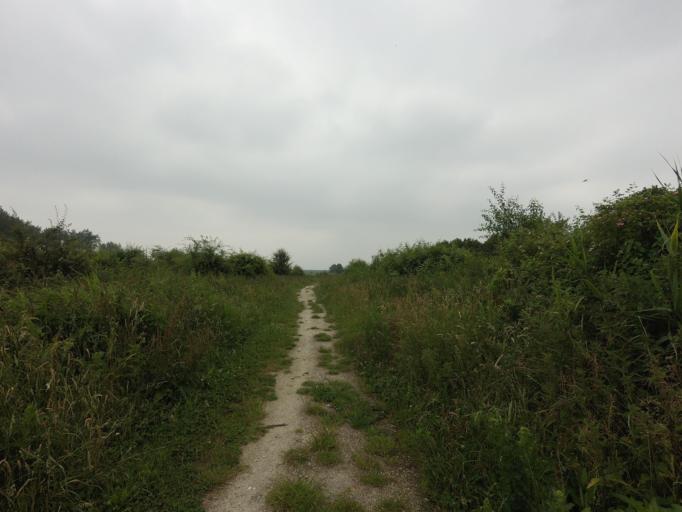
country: NL
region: Flevoland
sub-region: Gemeente Almere
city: Almere Stad
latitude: 52.4122
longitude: 5.3377
